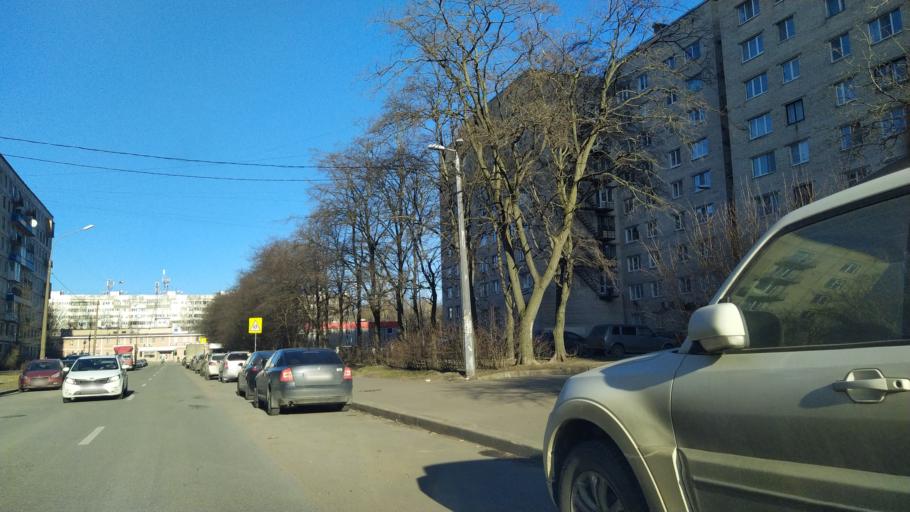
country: RU
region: St.-Petersburg
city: Grazhdanka
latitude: 60.0412
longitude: 30.4082
